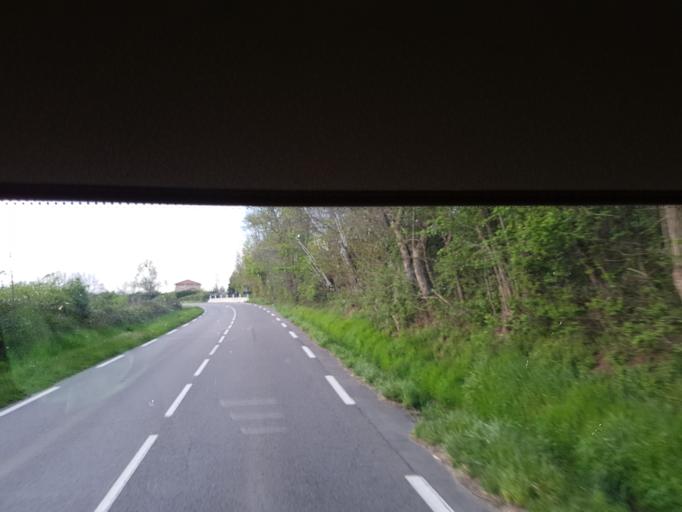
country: FR
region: Rhone-Alpes
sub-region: Departement du Rhone
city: Lentilly
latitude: 45.8046
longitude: 4.6682
